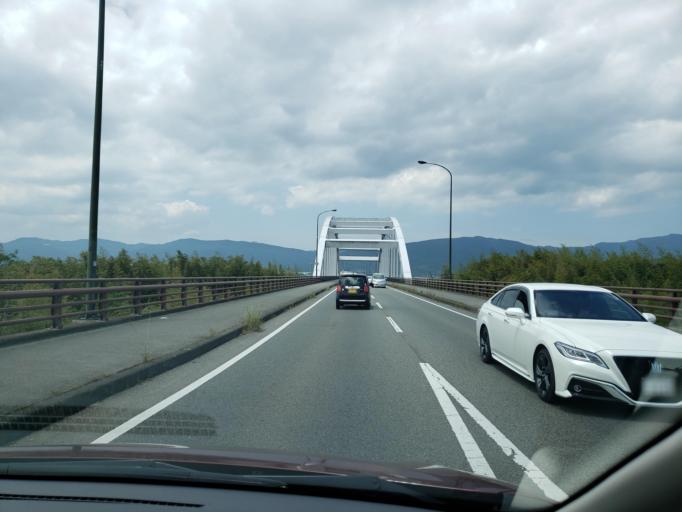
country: JP
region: Tokushima
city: Kamojimacho-jogejima
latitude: 34.0871
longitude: 134.3880
